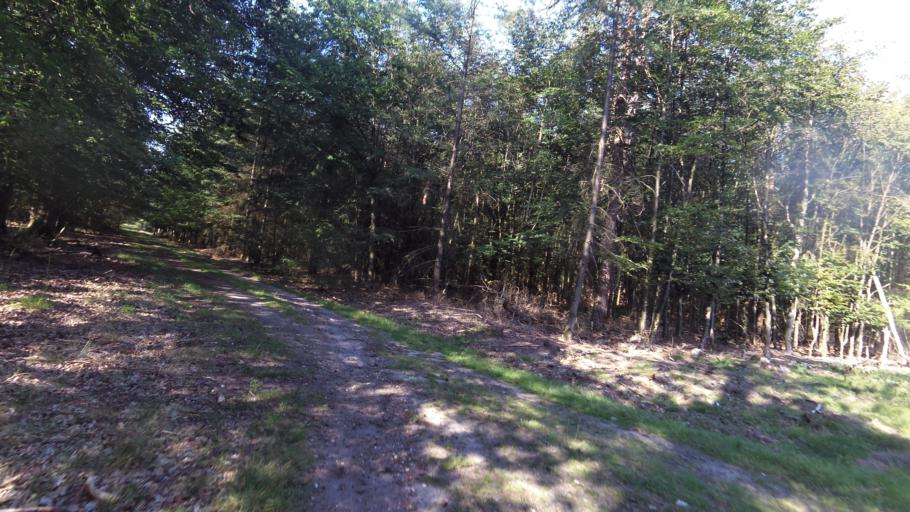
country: NL
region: Gelderland
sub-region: Gemeente Apeldoorn
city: Beekbergen
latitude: 52.1201
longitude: 5.9432
